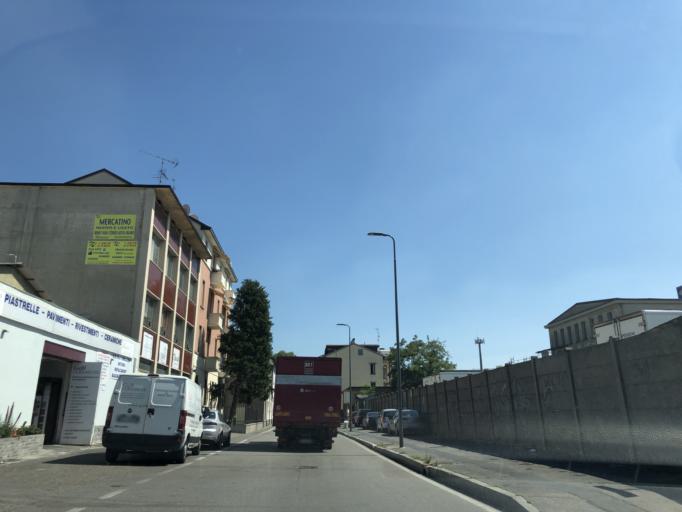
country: IT
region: Lombardy
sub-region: Citta metropolitana di Milano
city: Cormano
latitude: 45.5102
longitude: 9.1672
